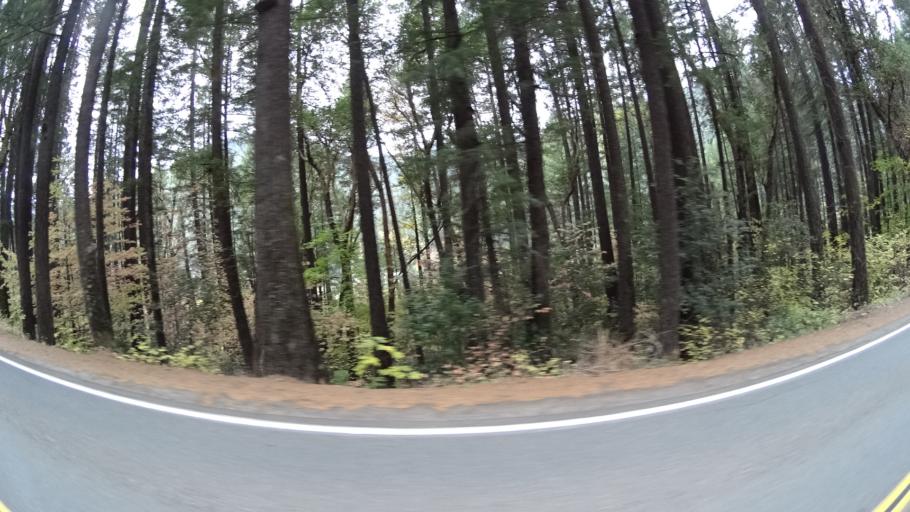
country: US
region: California
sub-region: Siskiyou County
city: Happy Camp
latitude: 41.8195
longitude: -123.3815
